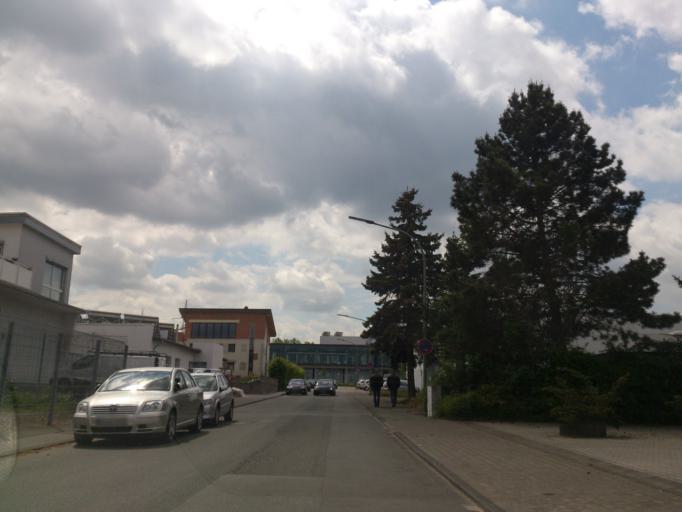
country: DE
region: North Rhine-Westphalia
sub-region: Regierungsbezirk Detmold
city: Paderborn
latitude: 51.7043
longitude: 8.7320
